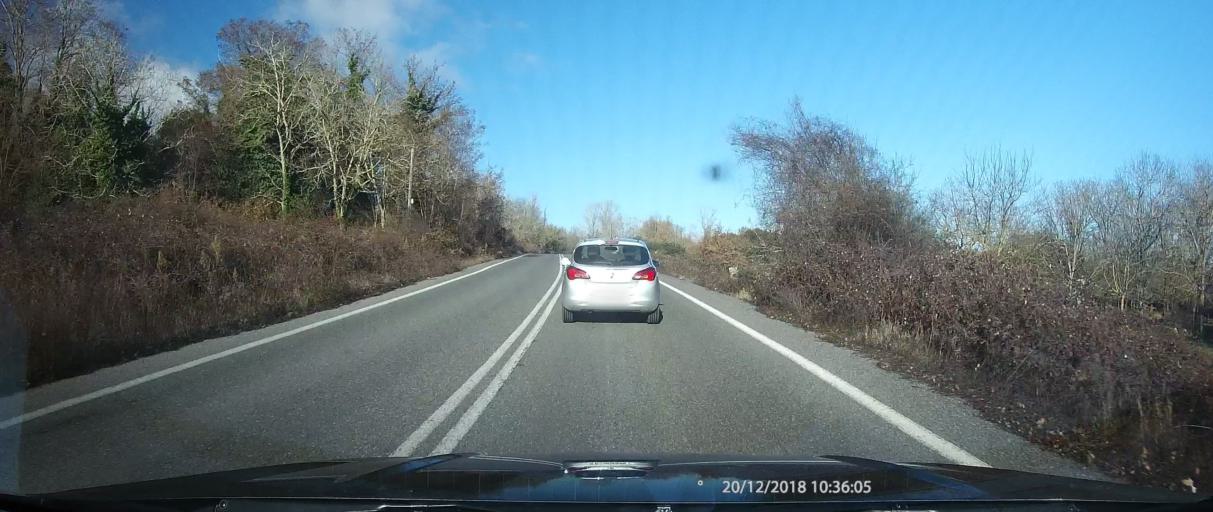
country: GR
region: Peloponnese
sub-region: Nomos Lakonias
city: Kariai
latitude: 37.3621
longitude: 22.4042
